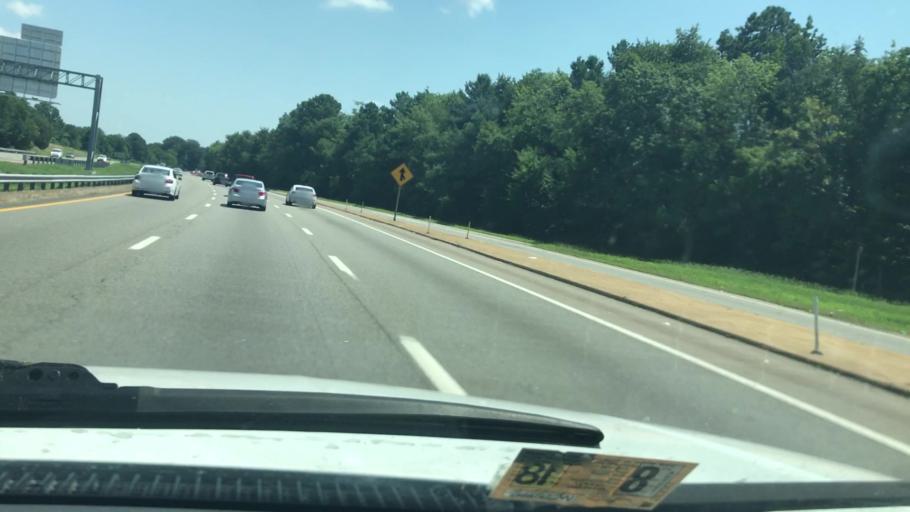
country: US
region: Virginia
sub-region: Henrico County
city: East Highland Park
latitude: 37.5551
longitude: -77.4082
